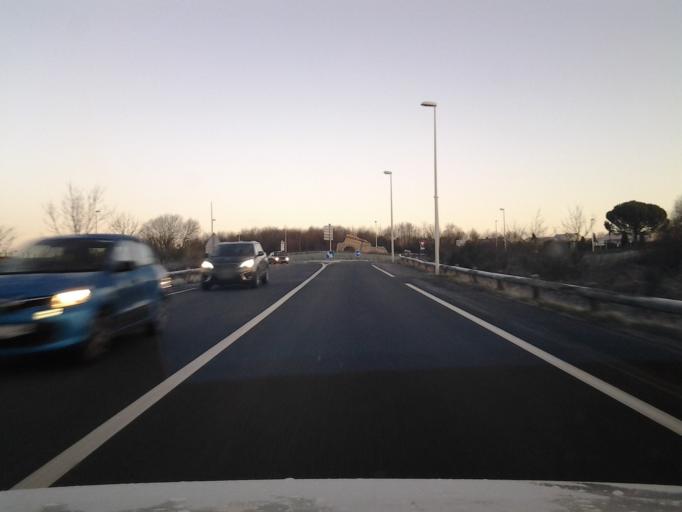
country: FR
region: Pays de la Loire
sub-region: Departement de la Vendee
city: Chambretaud
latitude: 46.9220
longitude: -0.9727
